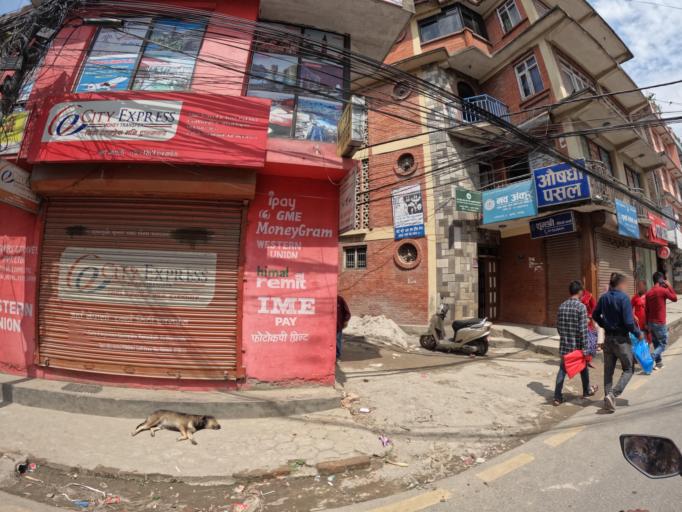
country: NP
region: Central Region
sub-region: Bagmati Zone
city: Bhaktapur
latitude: 27.6744
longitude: 85.3742
